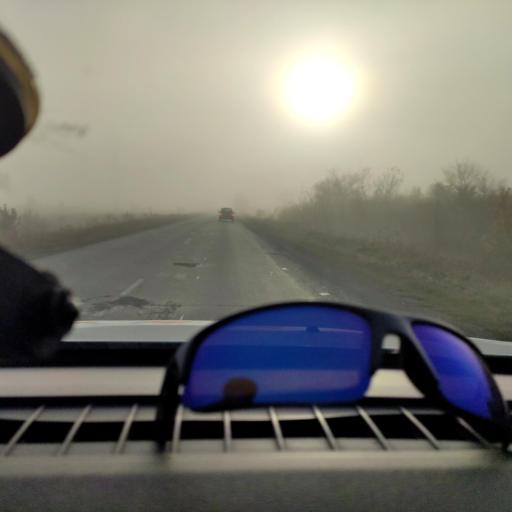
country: RU
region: Samara
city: Chapayevsk
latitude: 53.0008
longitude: 49.7611
